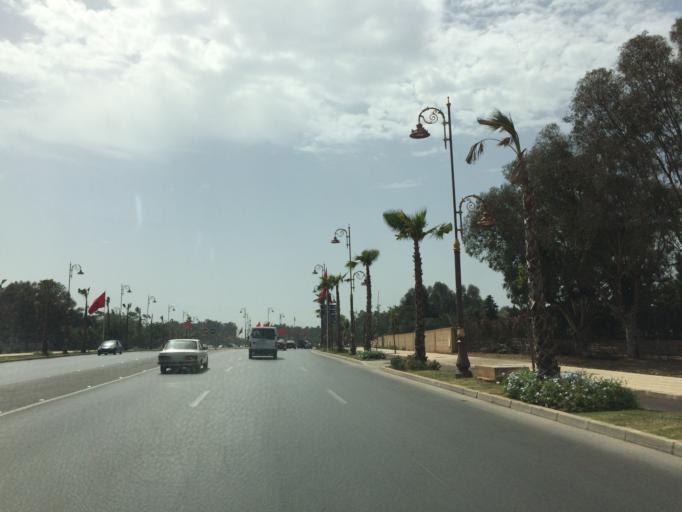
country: MA
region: Rabat-Sale-Zemmour-Zaer
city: Sale
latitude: 34.0329
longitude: -6.7730
